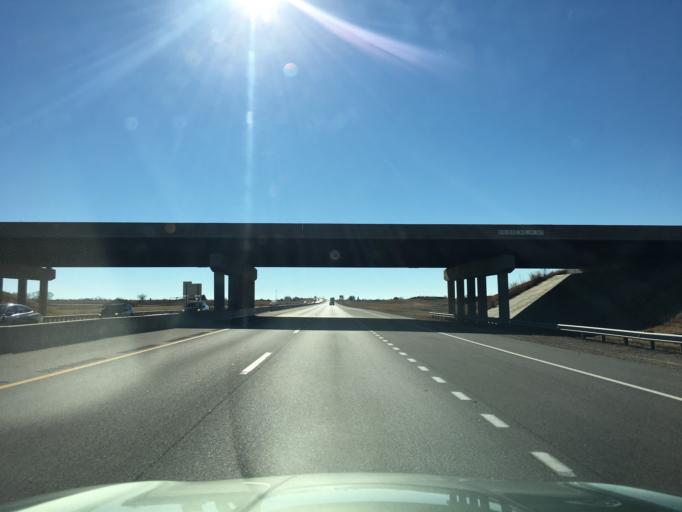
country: US
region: Kansas
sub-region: Sumner County
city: Wellington
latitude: 37.2767
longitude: -97.3404
